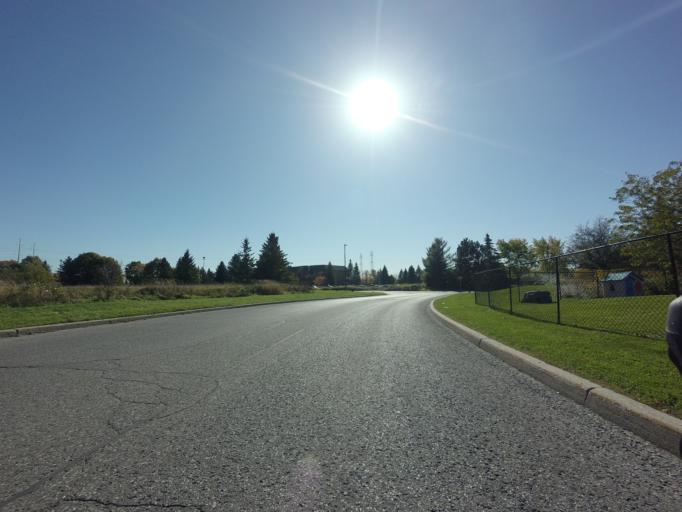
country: CA
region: Ontario
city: Bells Corners
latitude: 45.2880
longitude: -75.8710
